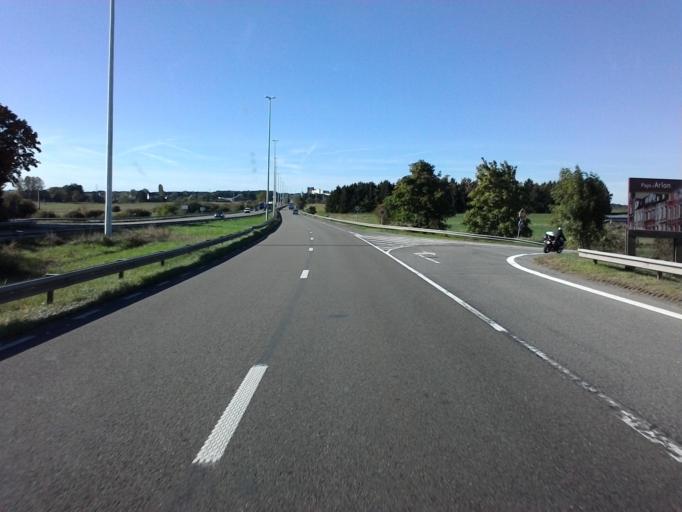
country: BE
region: Wallonia
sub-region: Province du Luxembourg
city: Aubange
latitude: 49.5740
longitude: 5.8202
